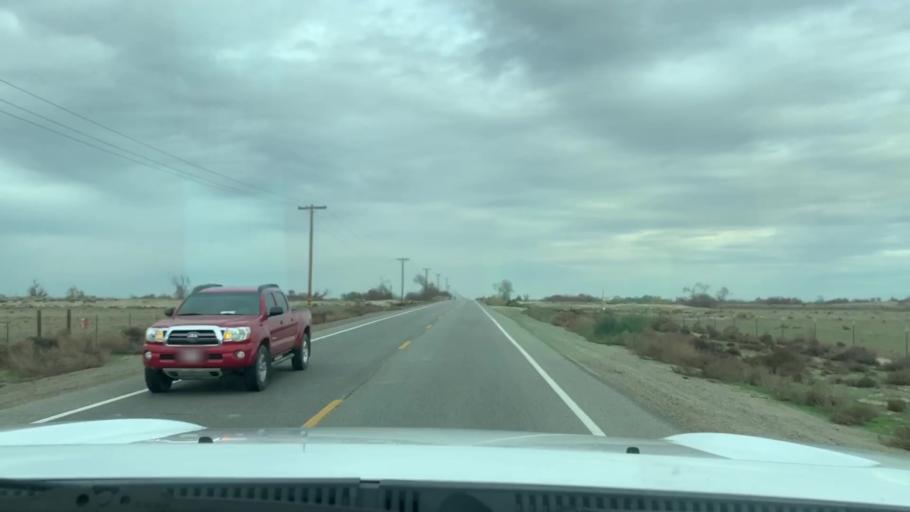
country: US
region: California
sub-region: Kern County
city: Rosedale
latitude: 35.3001
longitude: -119.2524
